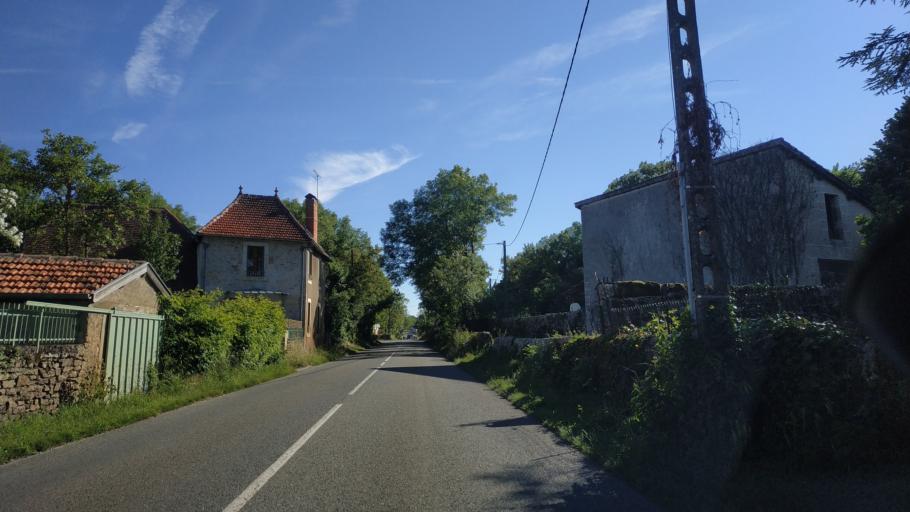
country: FR
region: Midi-Pyrenees
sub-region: Departement du Lot
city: Lacapelle-Marival
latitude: 44.6717
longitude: 1.8710
